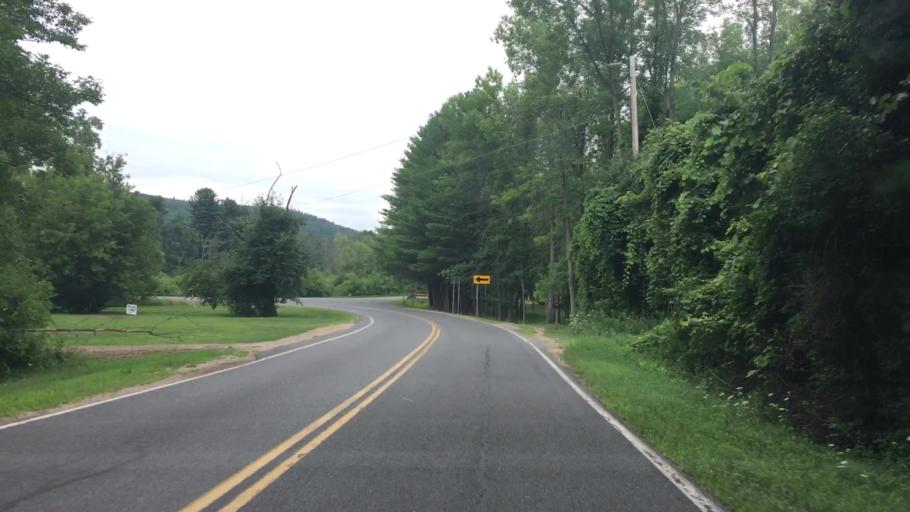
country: US
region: New York
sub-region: Clinton County
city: Peru
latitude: 44.5265
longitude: -73.5746
